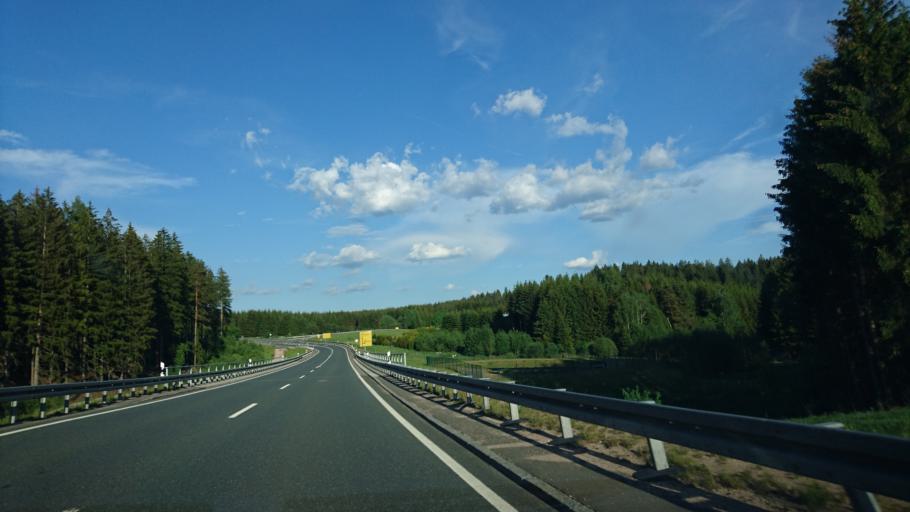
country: DE
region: Saxony
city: Stutzengrun
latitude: 50.5521
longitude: 12.5800
